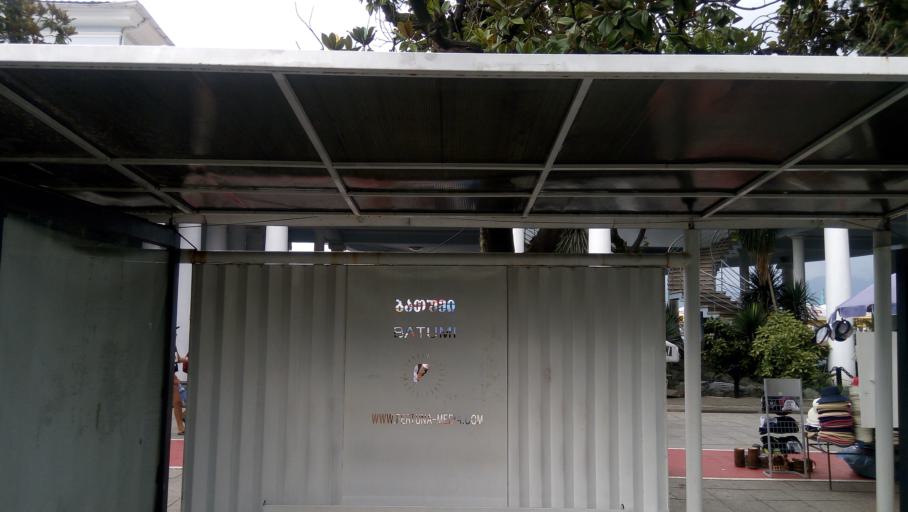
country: GE
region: Ajaria
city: Batumi
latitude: 41.6490
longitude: 41.6449
